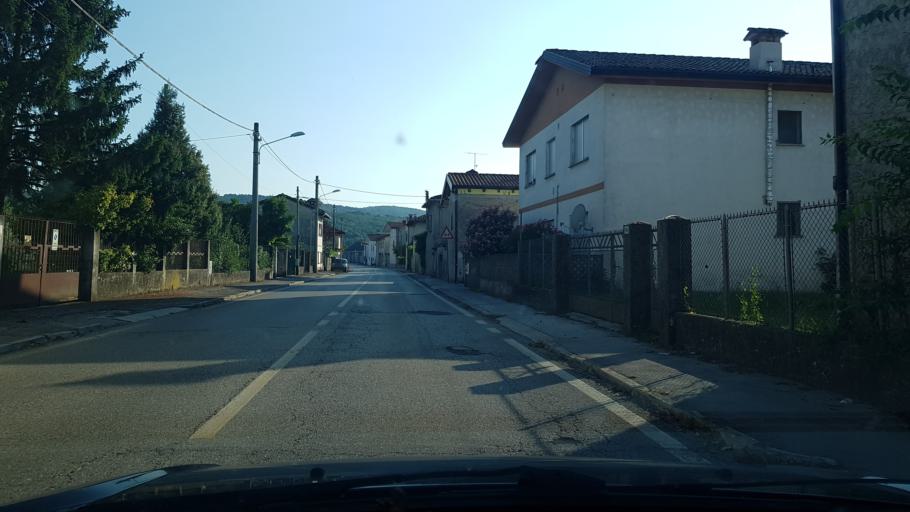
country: IT
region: Friuli Venezia Giulia
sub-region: Provincia di Gorizia
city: Savogna d'Isonzo
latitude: 45.9064
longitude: 13.5754
